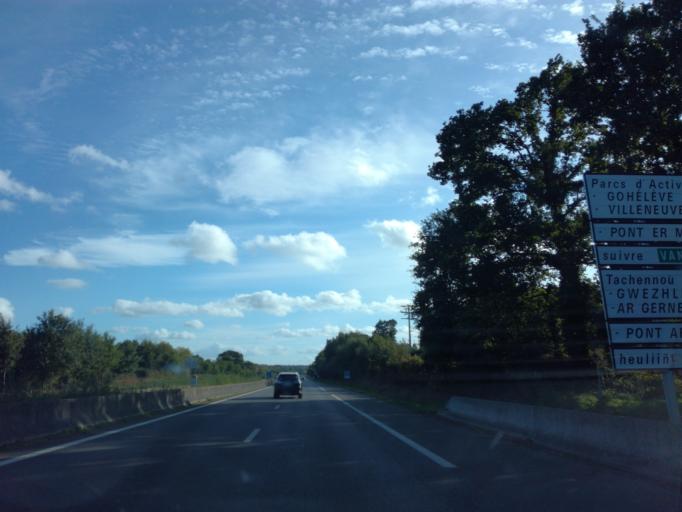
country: FR
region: Brittany
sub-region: Departement du Morbihan
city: Pontivy
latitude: 48.0643
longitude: -2.9431
